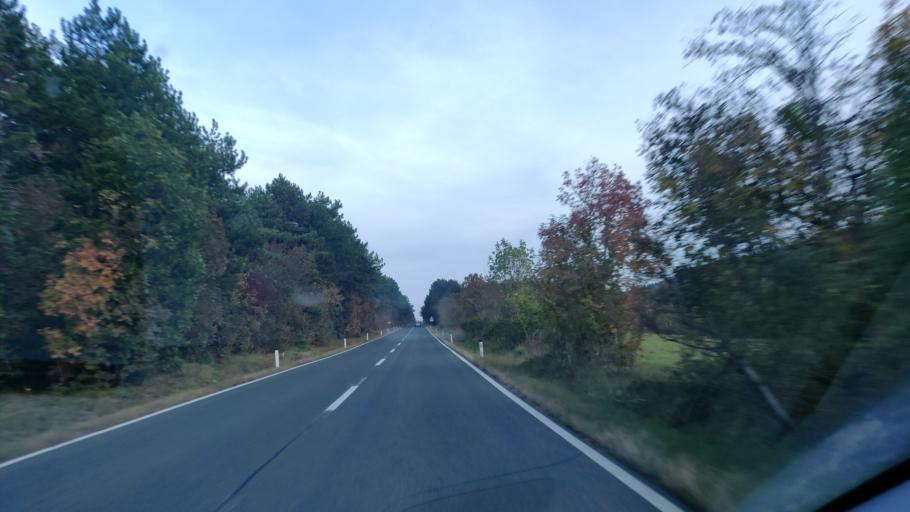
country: SI
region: Divaca
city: Divaca
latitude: 45.7388
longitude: 13.9419
